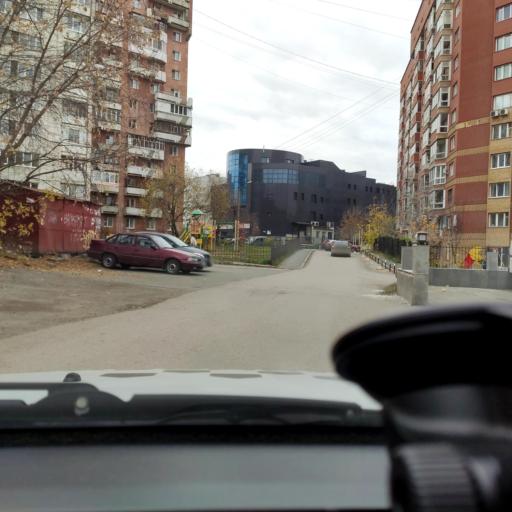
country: RU
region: Perm
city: Perm
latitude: 58.0069
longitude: 56.2751
